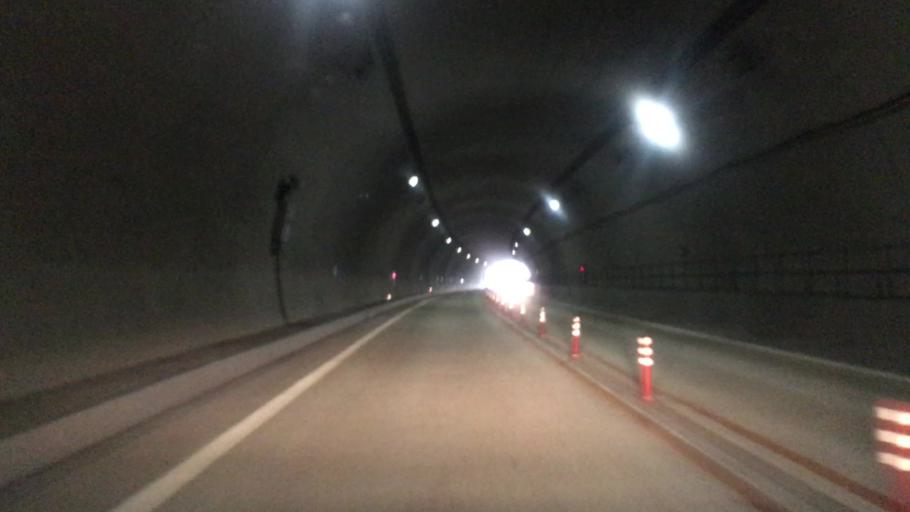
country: JP
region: Tottori
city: Tottori
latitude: 35.5658
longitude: 134.2884
